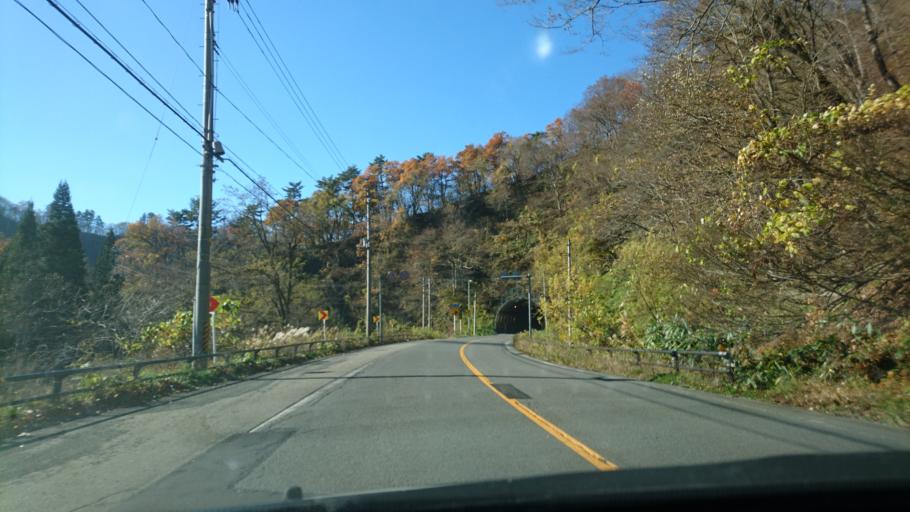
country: JP
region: Akita
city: Yokotemachi
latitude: 39.2827
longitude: 140.6709
